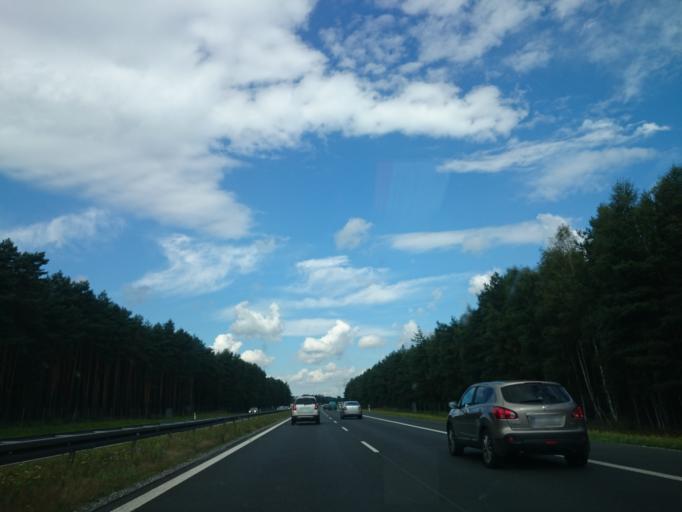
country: PL
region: Opole Voivodeship
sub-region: Powiat opolski
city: Proszkow
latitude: 50.5855
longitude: 17.8213
